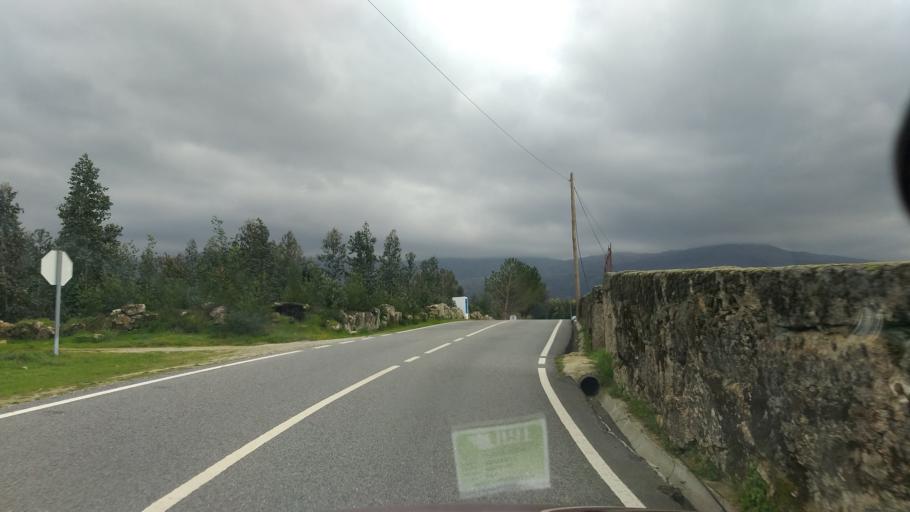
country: PT
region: Guarda
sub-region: Seia
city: Seia
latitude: 40.4780
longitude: -7.6499
